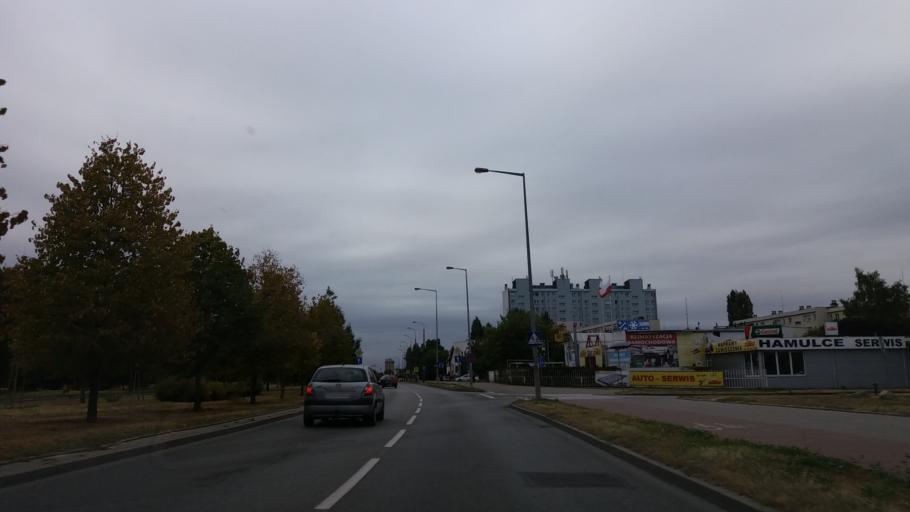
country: PL
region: Lubusz
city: Gorzow Wielkopolski
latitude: 52.7532
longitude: 15.2445
